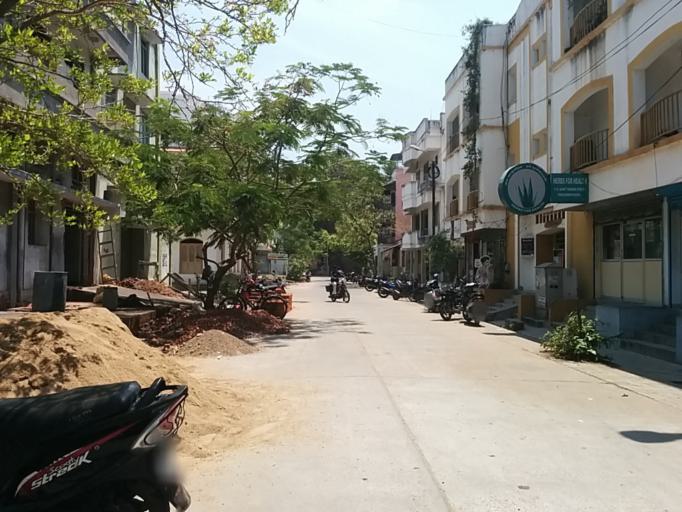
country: IN
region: Pondicherry
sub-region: Puducherry
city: Puducherry
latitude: 11.9321
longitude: 79.8307
